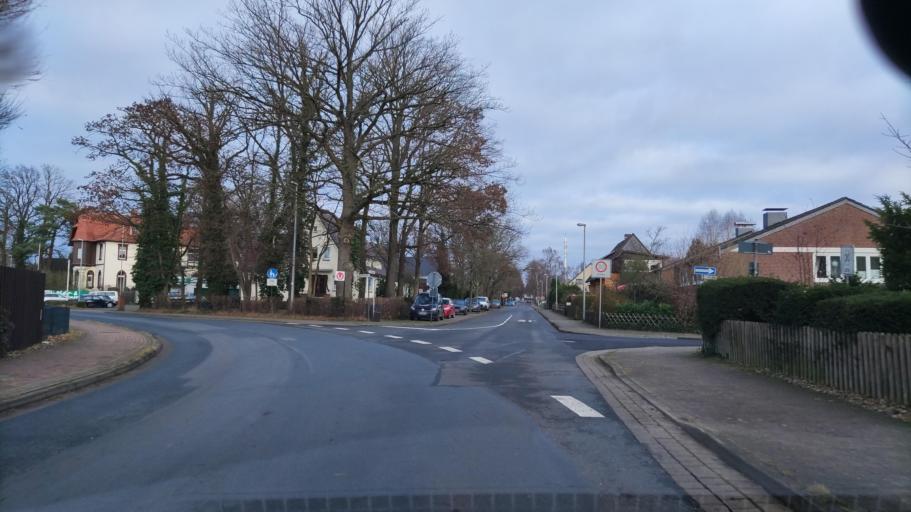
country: DE
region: Lower Saxony
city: Isernhagen Farster Bauerschaft
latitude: 52.4970
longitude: 9.8552
